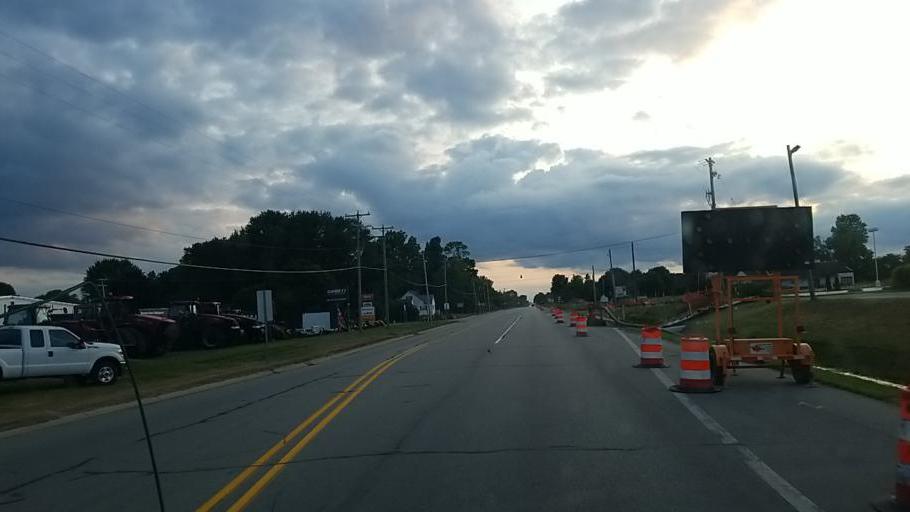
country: US
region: Michigan
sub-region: Newaygo County
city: Fremont
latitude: 43.4672
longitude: -85.9781
